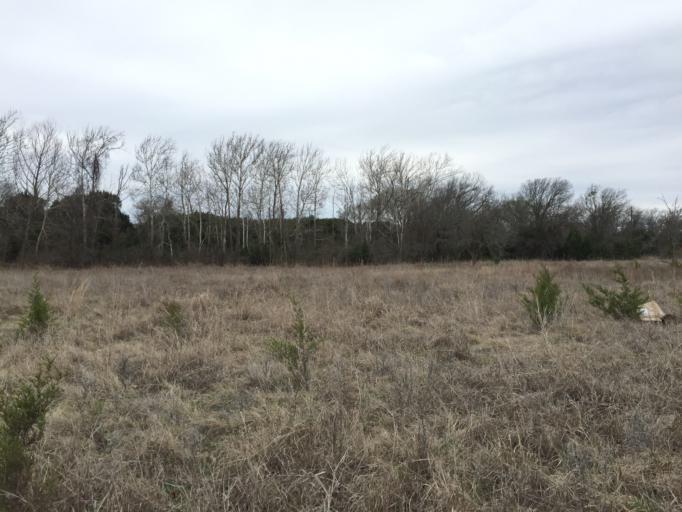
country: US
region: Texas
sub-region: Bell County
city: Fort Hood
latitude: 31.1159
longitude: -97.8120
